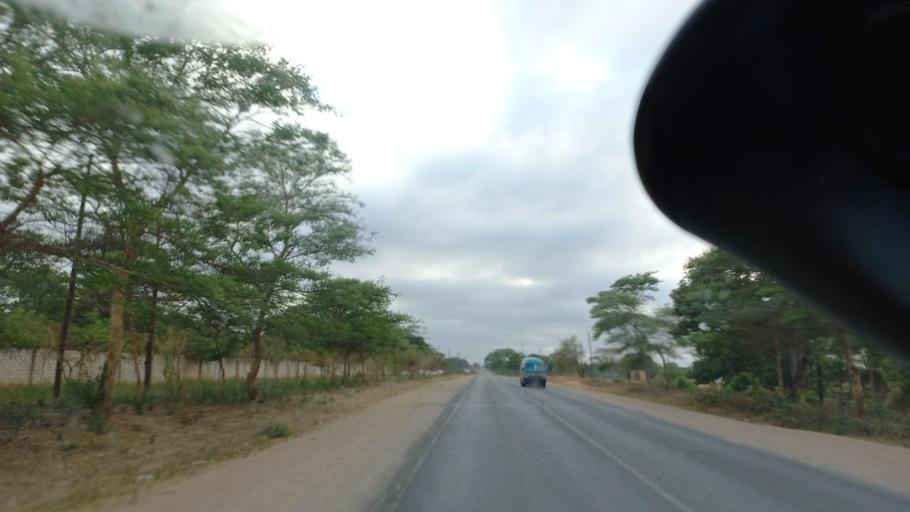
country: ZM
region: Lusaka
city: Chongwe
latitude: -15.3477
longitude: 28.5032
